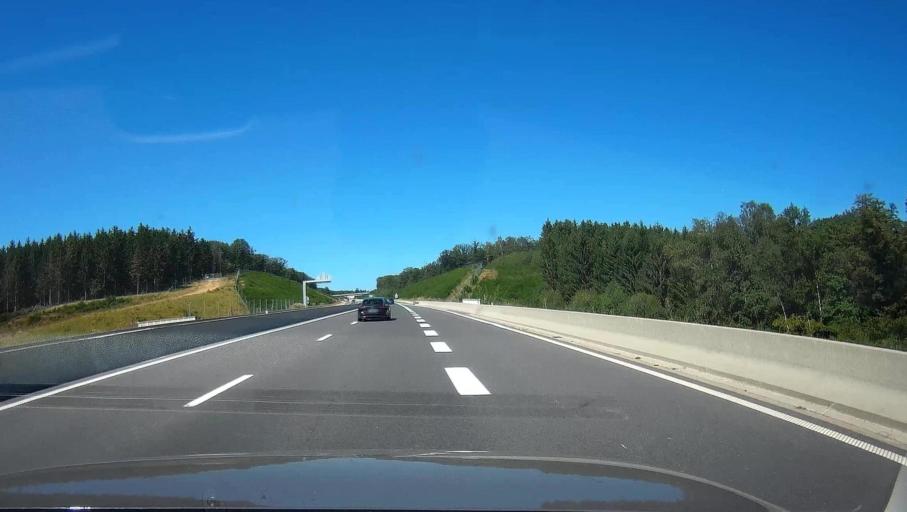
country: FR
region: Champagne-Ardenne
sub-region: Departement des Ardennes
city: Rimogne
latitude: 49.8490
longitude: 4.5137
